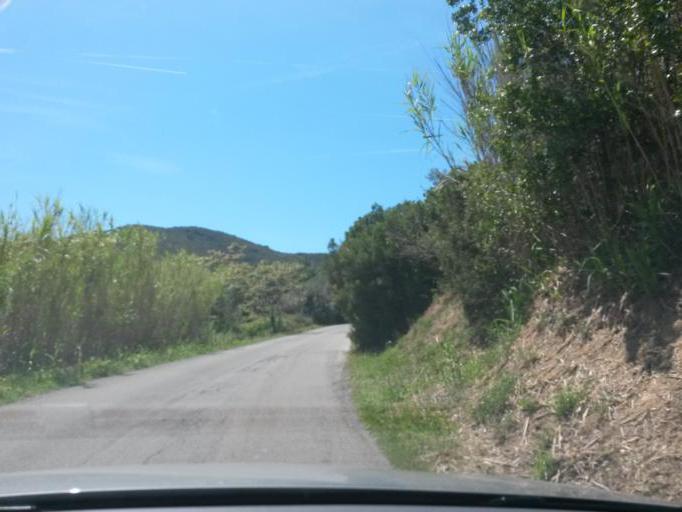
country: IT
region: Tuscany
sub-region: Provincia di Livorno
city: Portoferraio
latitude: 42.8167
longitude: 10.3025
